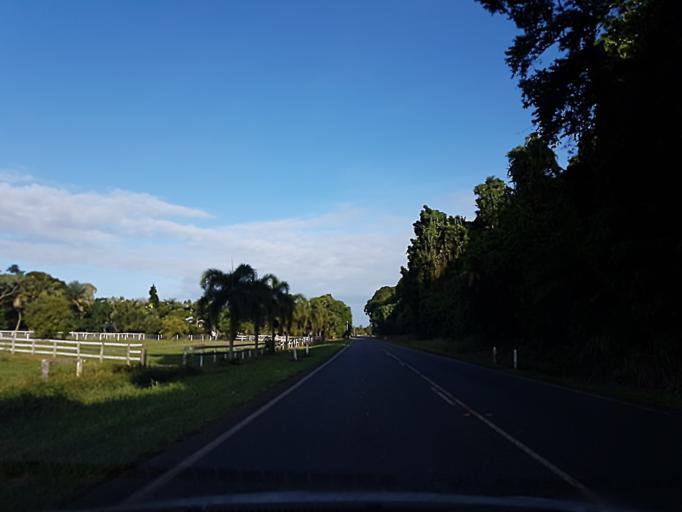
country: AU
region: Queensland
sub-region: Cairns
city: Port Douglas
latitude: -16.3562
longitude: 145.4090
